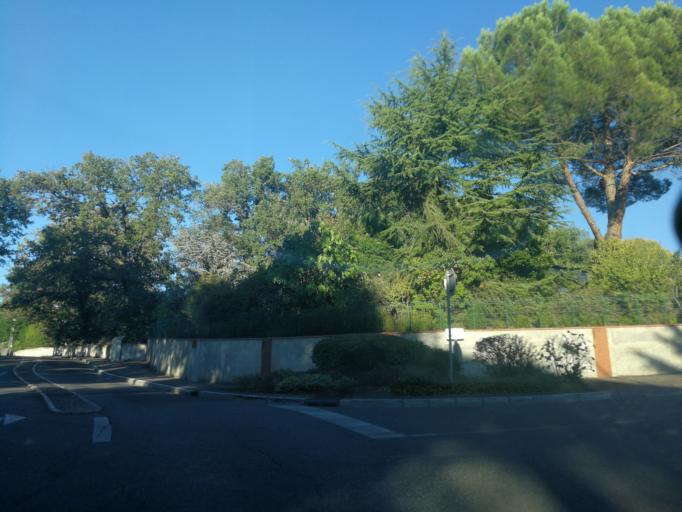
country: FR
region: Midi-Pyrenees
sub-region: Departement de la Haute-Garonne
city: Balma
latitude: 43.6127
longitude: 1.5019
